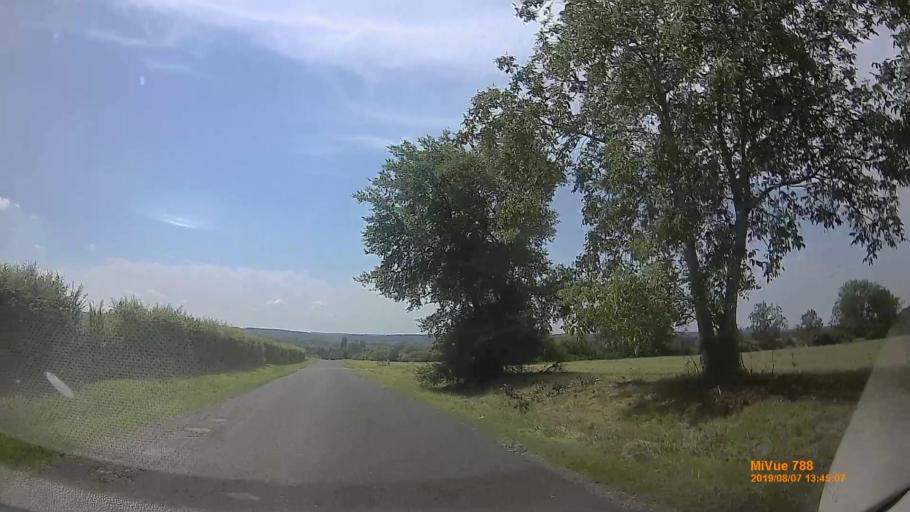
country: HU
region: Zala
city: Cserszegtomaj
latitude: 46.8856
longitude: 17.2069
